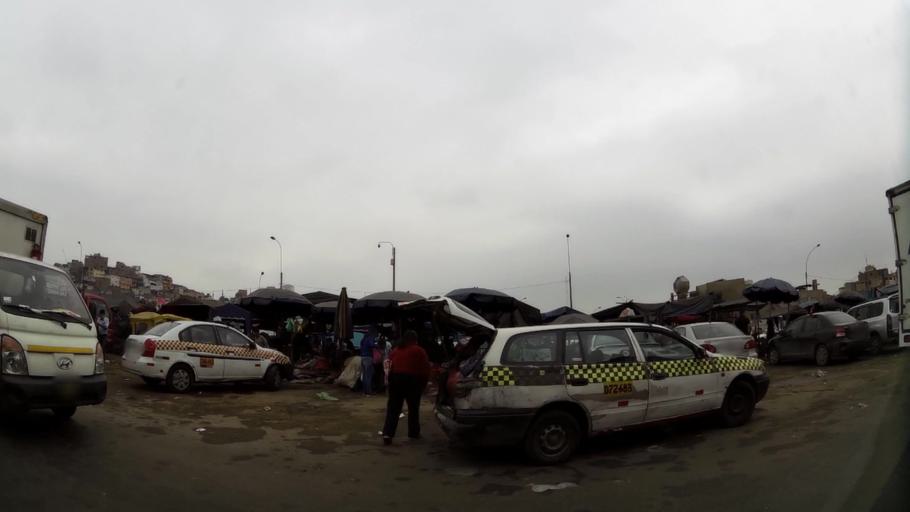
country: PE
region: Lima
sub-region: Lima
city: San Luis
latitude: -12.0586
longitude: -77.0061
